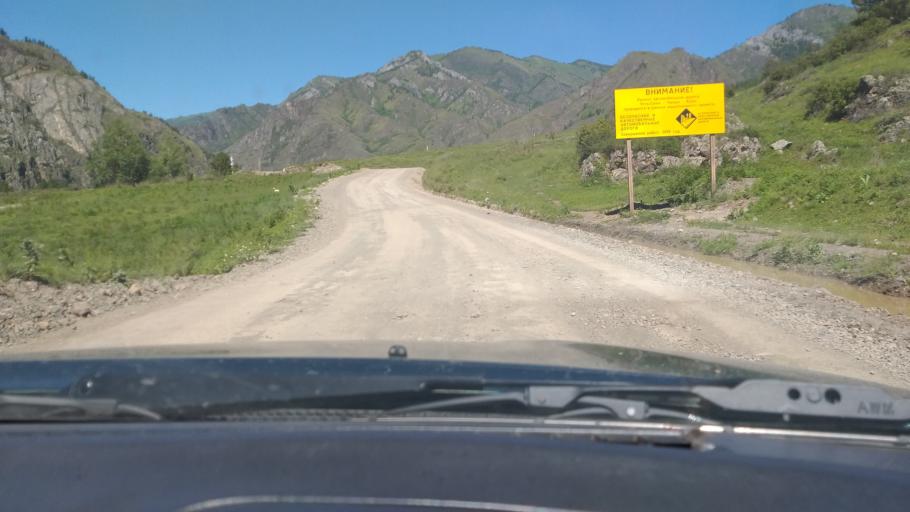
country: RU
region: Altay
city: Chemal
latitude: 51.2085
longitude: 86.0865
